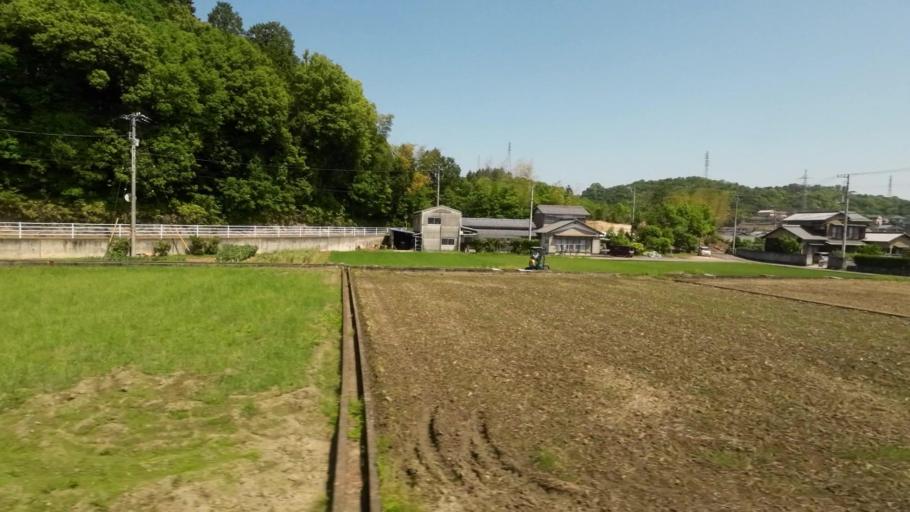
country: JP
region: Ehime
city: Niihama
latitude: 33.9280
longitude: 133.2646
